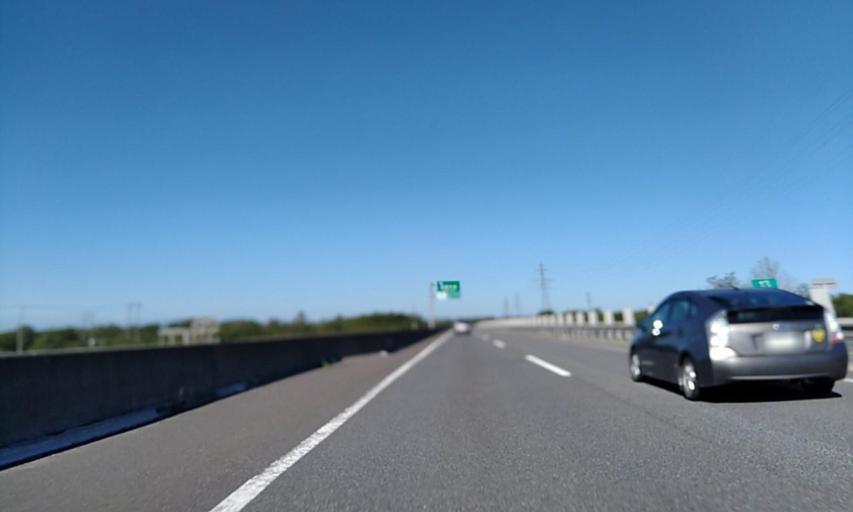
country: JP
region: Hokkaido
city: Tomakomai
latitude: 42.6689
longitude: 141.7958
